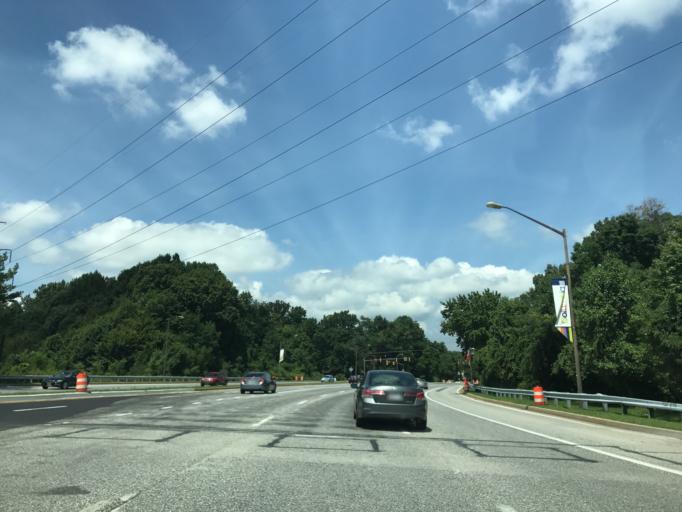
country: US
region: Maryland
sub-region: Howard County
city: Riverside
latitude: 39.2054
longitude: -76.8655
